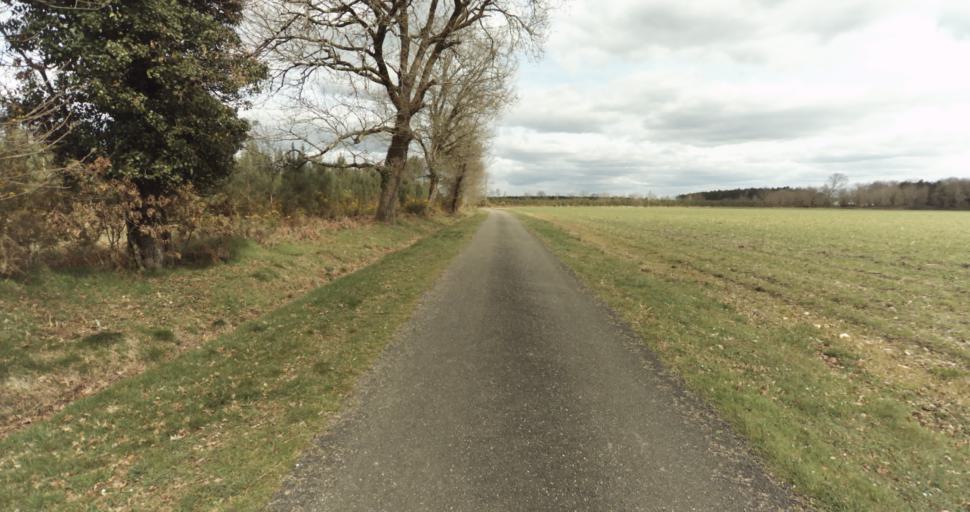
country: FR
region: Aquitaine
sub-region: Departement des Landes
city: Roquefort
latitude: 44.0776
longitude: -0.4126
